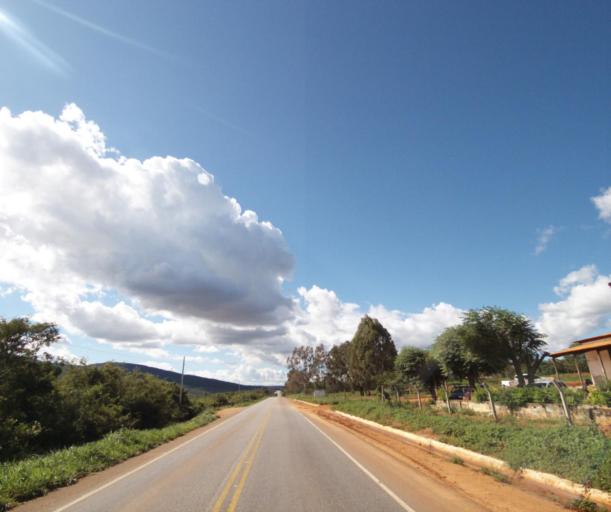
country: BR
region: Bahia
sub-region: Caetite
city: Caetite
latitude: -14.1038
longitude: -42.4419
